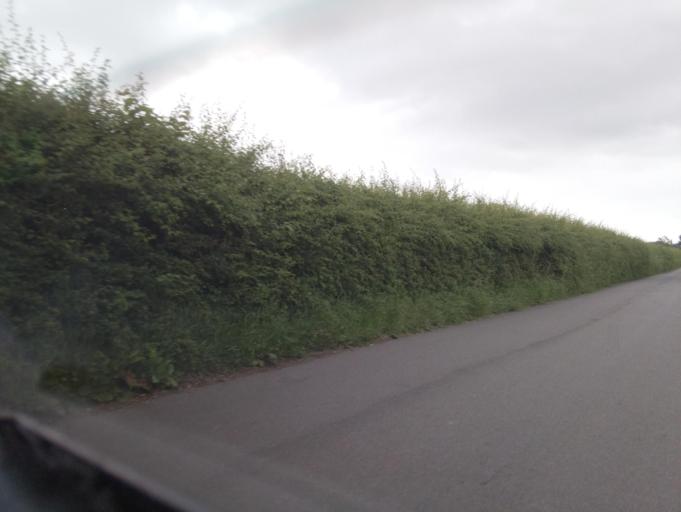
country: GB
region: England
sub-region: Derbyshire
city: Rodsley
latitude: 52.8750
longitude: -1.7140
